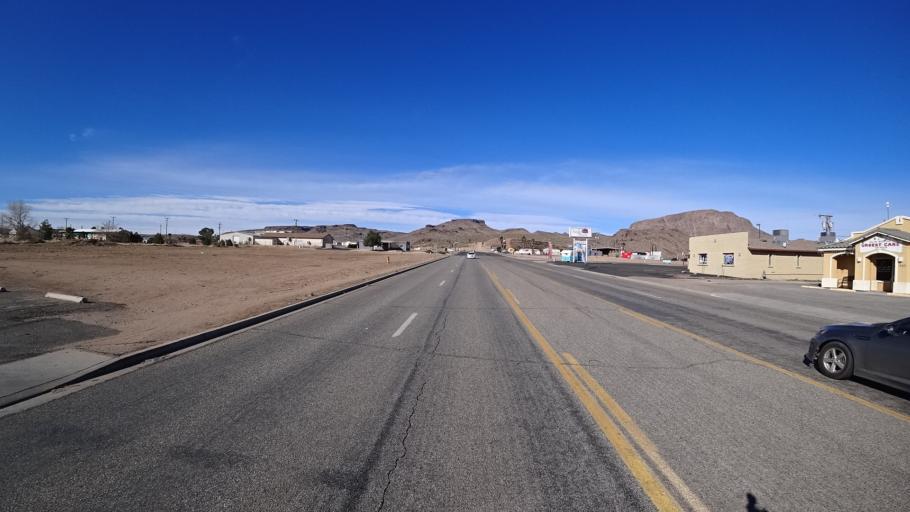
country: US
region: Arizona
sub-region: Mohave County
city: New Kingman-Butler
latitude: 35.2538
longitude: -114.0355
